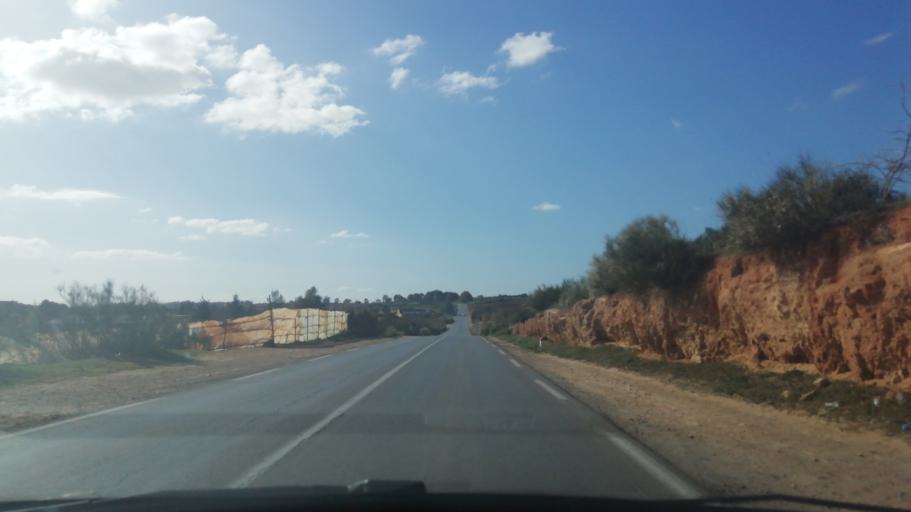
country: DZ
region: Mostaganem
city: Mostaganem
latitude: 35.9553
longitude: 0.2382
